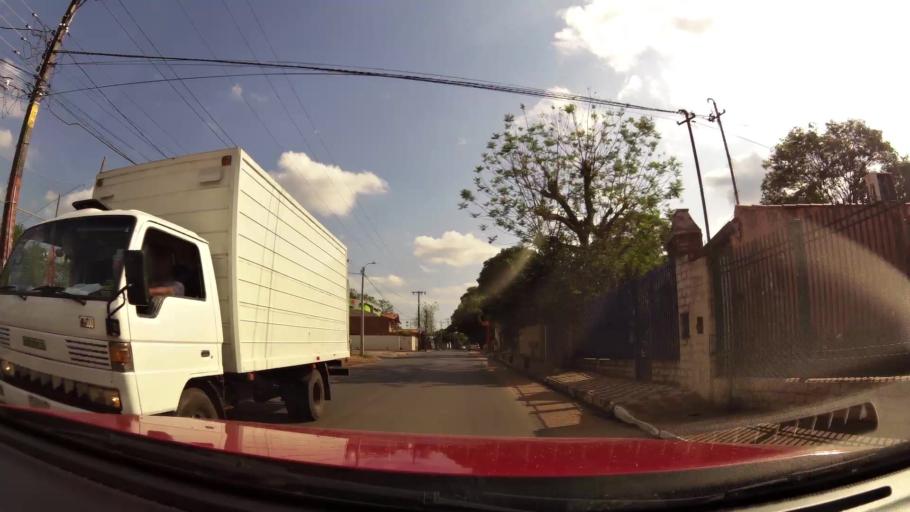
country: PY
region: Central
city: Fernando de la Mora
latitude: -25.3208
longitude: -57.5283
